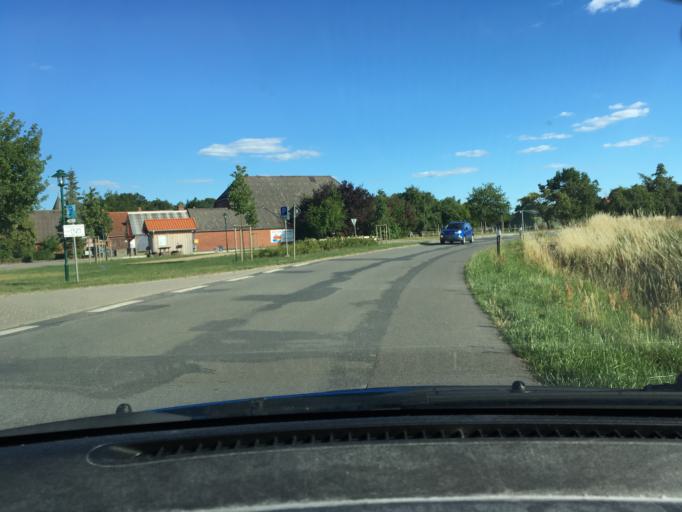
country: DE
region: Mecklenburg-Vorpommern
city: Boizenburg
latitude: 53.3457
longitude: 10.7238
